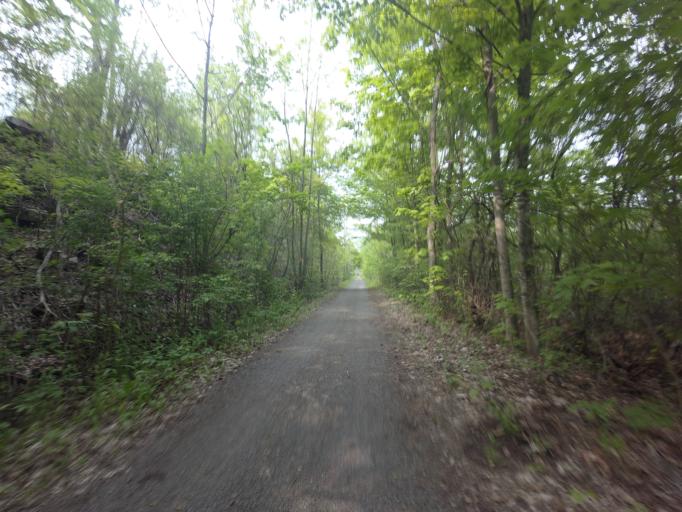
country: CA
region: Ontario
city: Kingston
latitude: 44.4114
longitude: -76.6281
